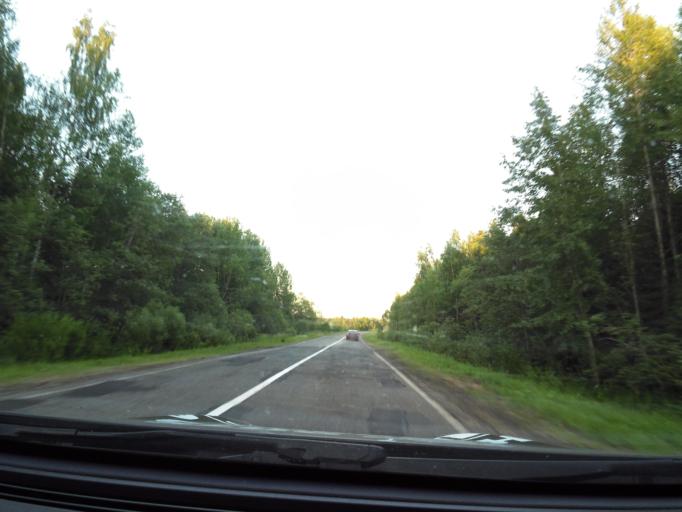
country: RU
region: Jaroslavl
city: Prechistoye
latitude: 58.3825
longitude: 40.4685
